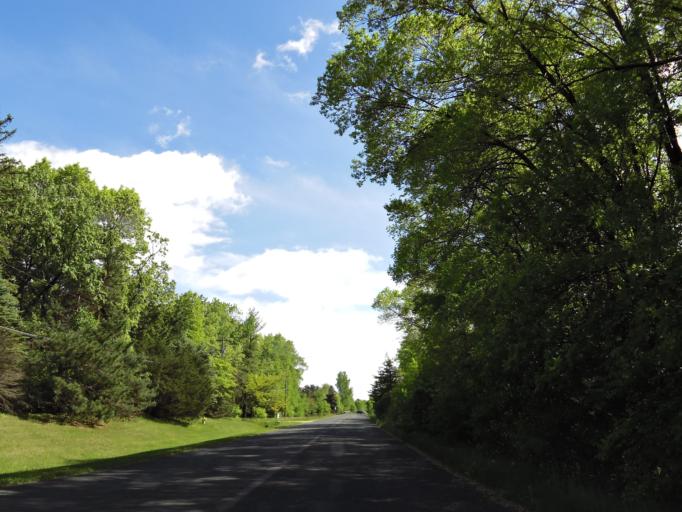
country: US
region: Minnesota
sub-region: Washington County
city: Lakeland
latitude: 44.9676
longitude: -92.7716
